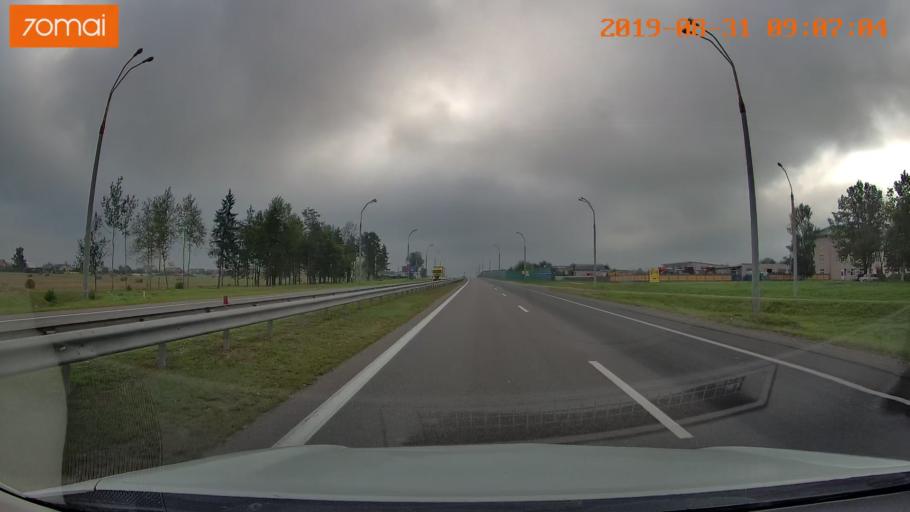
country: BY
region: Minsk
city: Chervyen'
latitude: 53.7278
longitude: 28.4253
